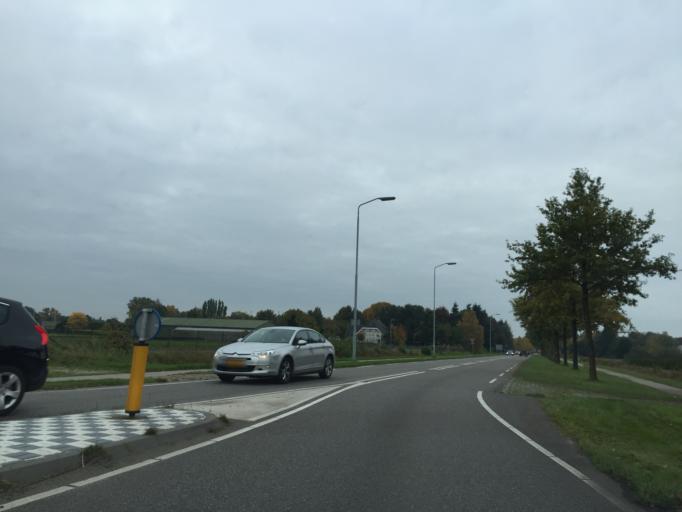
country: NL
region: North Brabant
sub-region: Gemeente Waalwijk
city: Waalwijk
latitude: 51.6652
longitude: 5.0534
